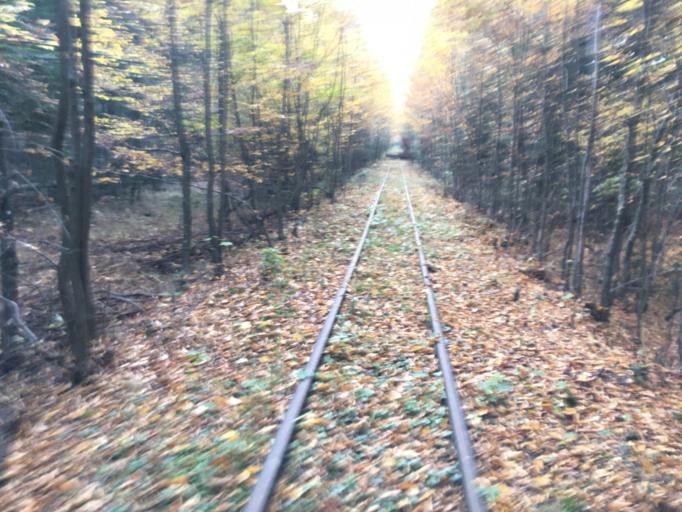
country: PL
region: Swietokrzyskie
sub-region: Powiat starachowicki
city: Brody
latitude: 51.0748
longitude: 21.1633
